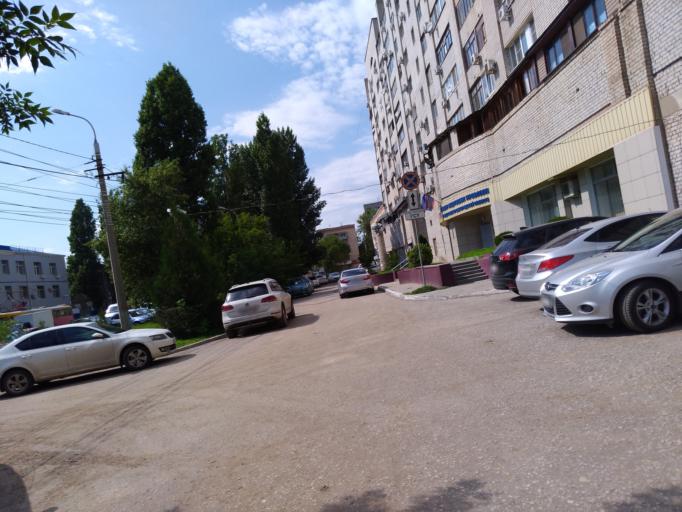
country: RU
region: Volgograd
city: Volgograd
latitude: 48.7125
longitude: 44.5011
